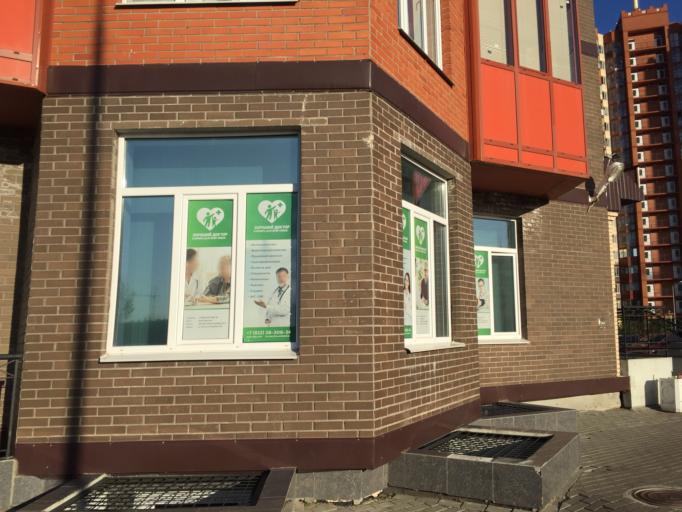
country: RU
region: Leningrad
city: Murino
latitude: 60.0641
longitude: 30.4566
